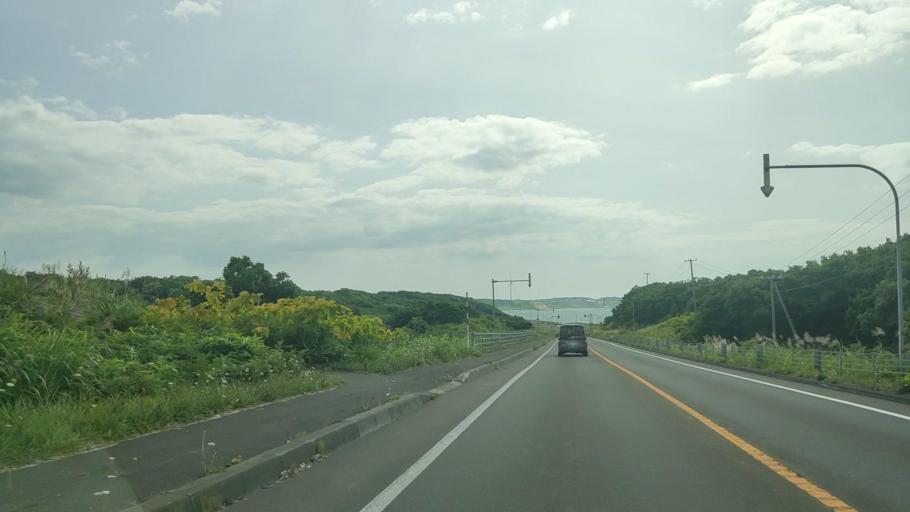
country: JP
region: Hokkaido
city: Rumoi
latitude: 44.3401
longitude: 141.6843
